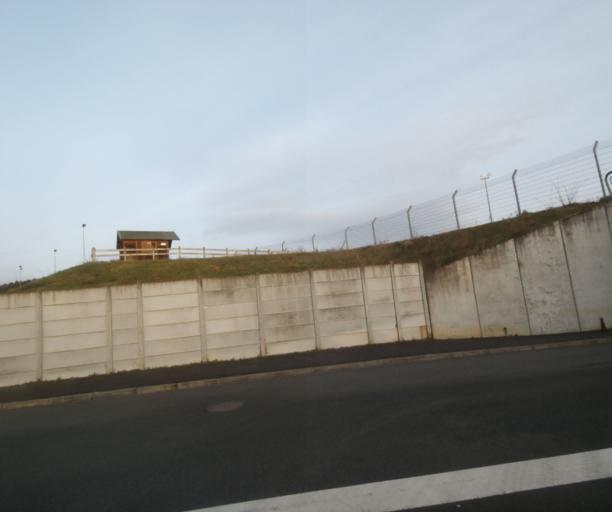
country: FR
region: Pays de la Loire
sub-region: Departement de la Sarthe
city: Le Mans
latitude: 47.9608
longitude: 0.2231
